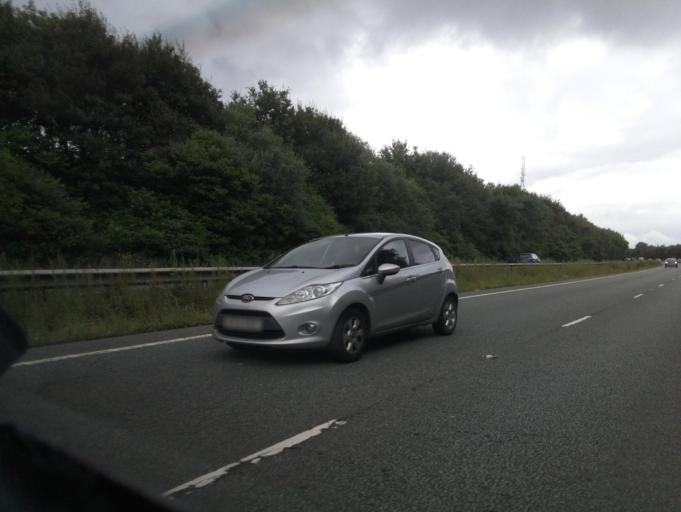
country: GB
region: England
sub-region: Leicestershire
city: Market Harborough
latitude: 52.4074
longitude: -0.9614
